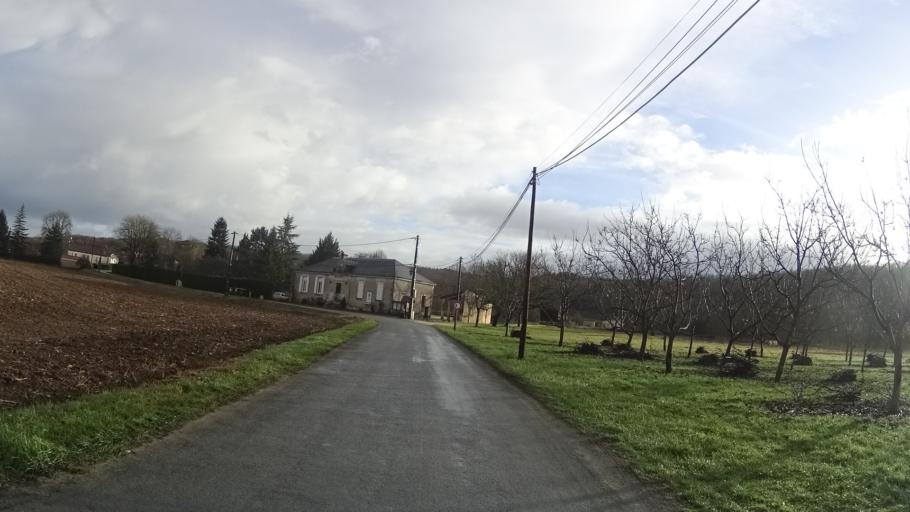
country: FR
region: Aquitaine
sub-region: Departement de la Dordogne
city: Sorges
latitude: 45.2432
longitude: 0.8938
